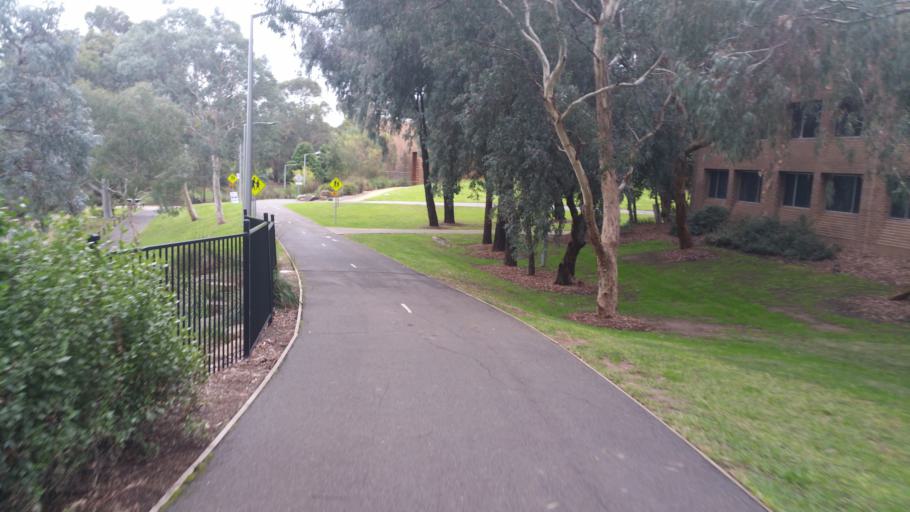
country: AU
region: Victoria
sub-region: Monash
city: Notting Hill
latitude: -37.9076
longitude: 145.1388
